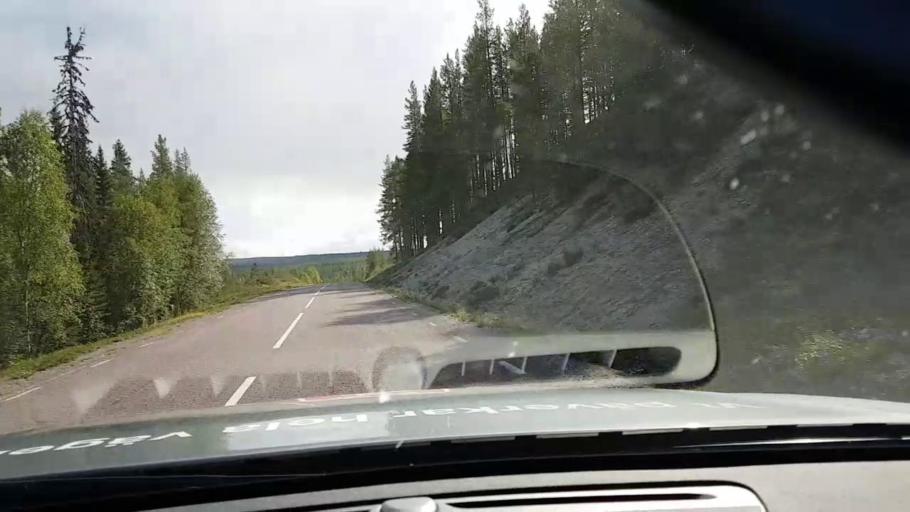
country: SE
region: Vaesterbotten
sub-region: Asele Kommun
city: Asele
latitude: 63.8745
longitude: 17.3567
